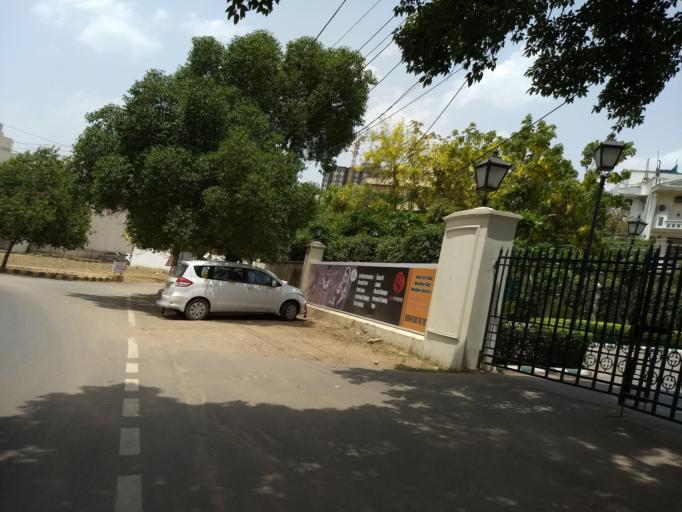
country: IN
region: Haryana
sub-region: Gurgaon
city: Gurgaon
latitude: 28.4951
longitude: 77.1038
